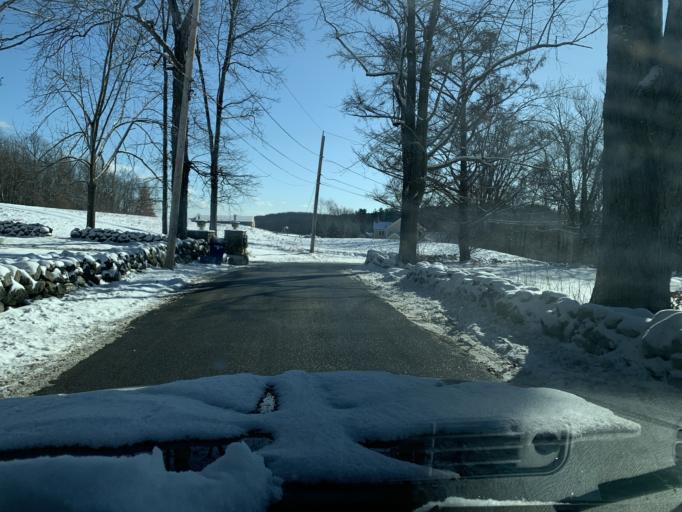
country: US
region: Massachusetts
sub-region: Essex County
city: Topsfield
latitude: 42.6311
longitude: -70.9539
